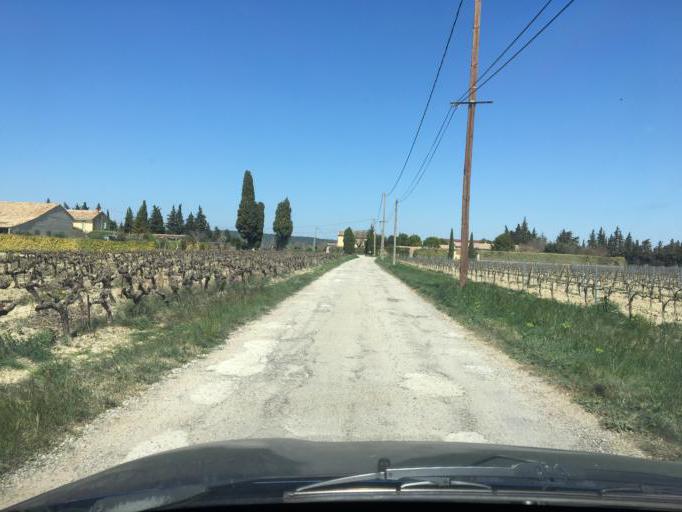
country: FR
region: Provence-Alpes-Cote d'Azur
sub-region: Departement du Vaucluse
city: Serignan-du-Comtat
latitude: 44.1714
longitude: 4.8460
